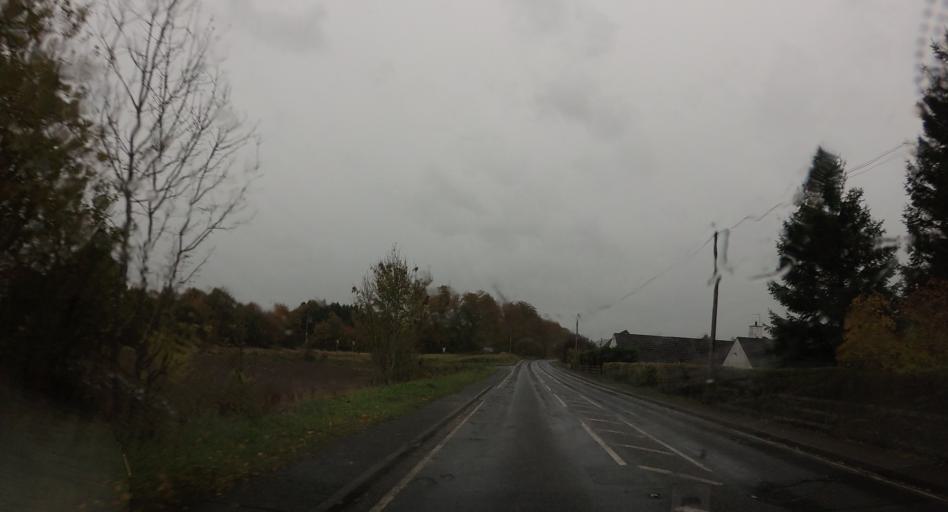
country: GB
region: Scotland
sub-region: Perth and Kinross
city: Coupar Angus
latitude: 56.5387
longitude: -3.2566
